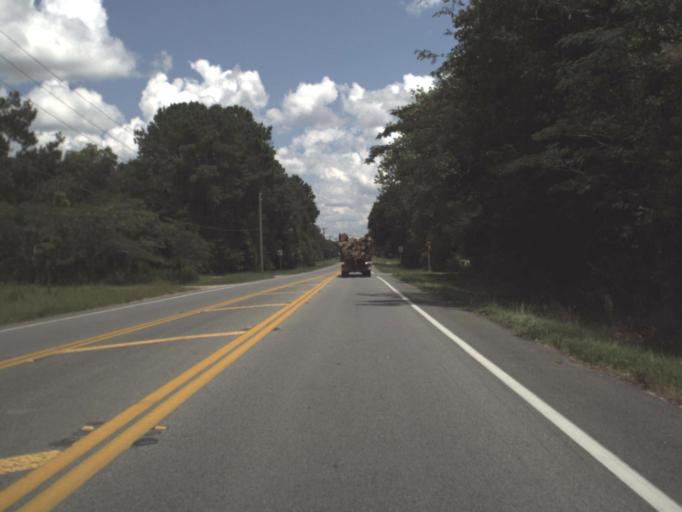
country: US
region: Florida
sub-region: Taylor County
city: Perry
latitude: 30.1052
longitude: -83.6071
